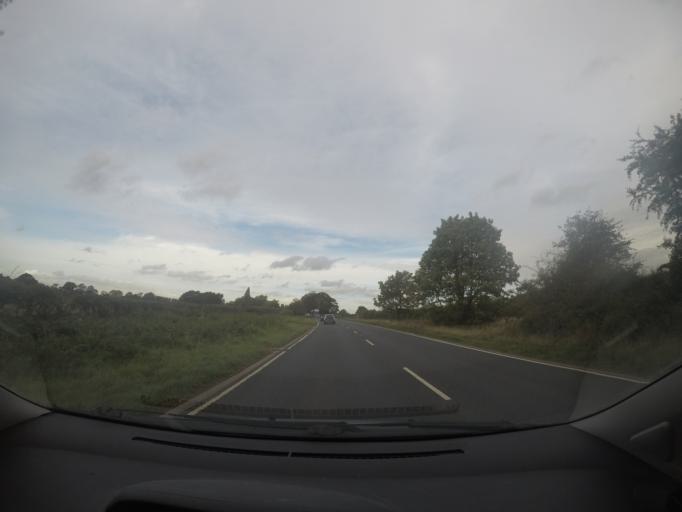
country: GB
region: England
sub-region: City of York
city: Deighton
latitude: 53.9000
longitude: -1.0476
